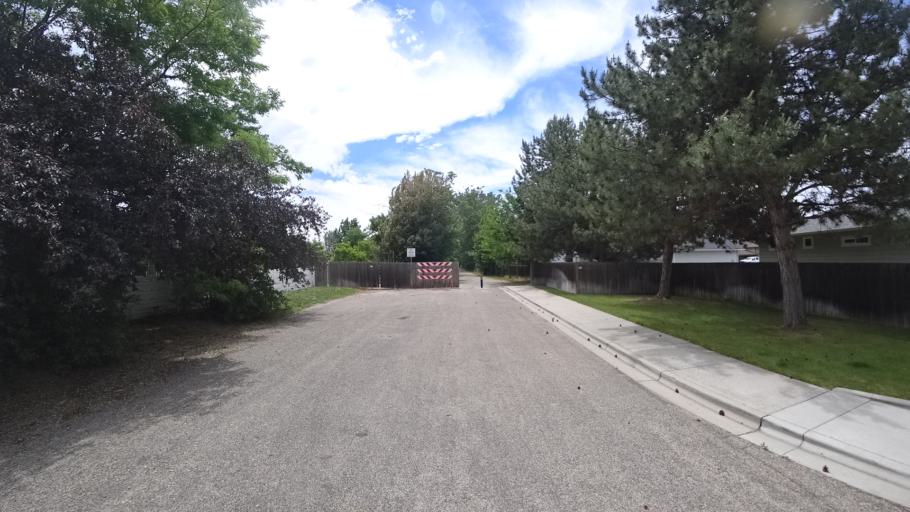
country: US
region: Idaho
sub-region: Ada County
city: Eagle
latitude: 43.6332
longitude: -116.3245
